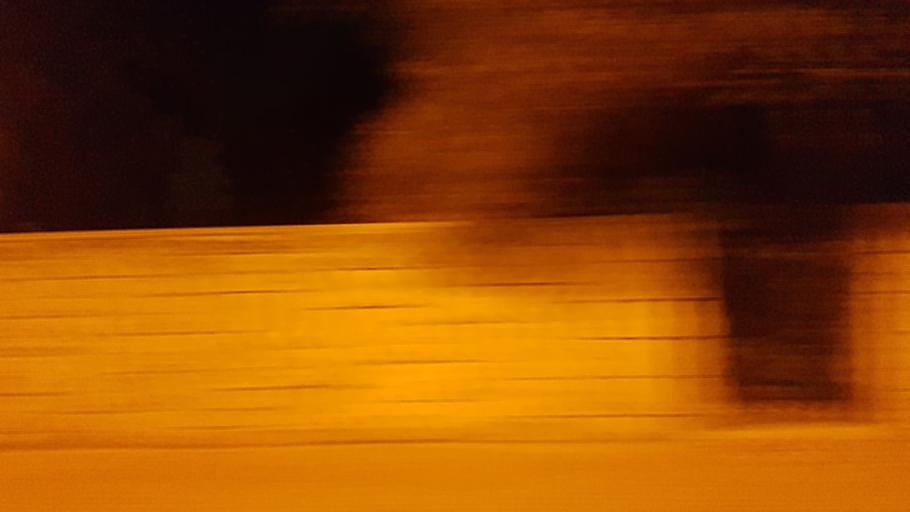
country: IL
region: Central District
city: Hod HaSharon
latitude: 32.1665
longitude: 34.8938
